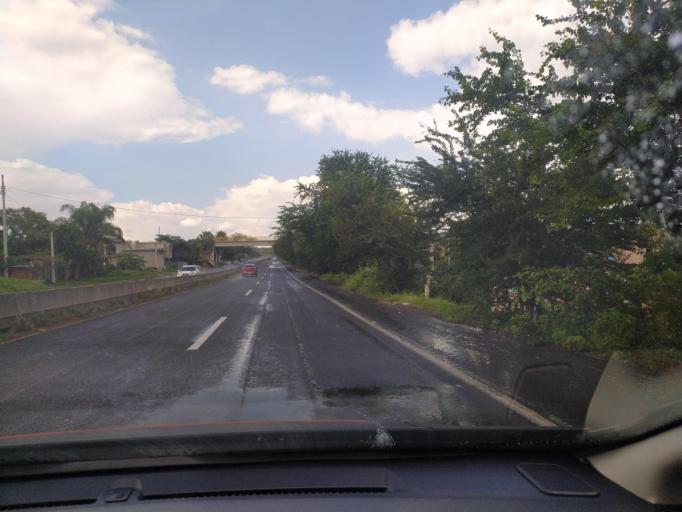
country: MX
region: Jalisco
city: Bellavista
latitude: 20.4277
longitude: -103.6043
